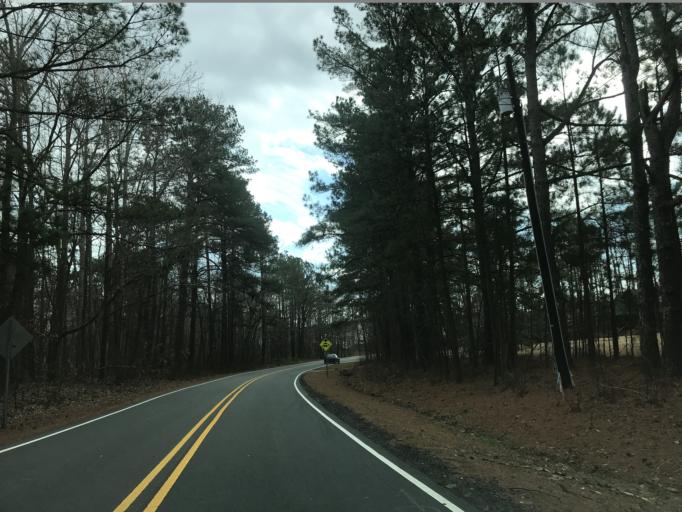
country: US
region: North Carolina
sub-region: Wake County
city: Morrisville
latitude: 35.7880
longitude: -78.8568
